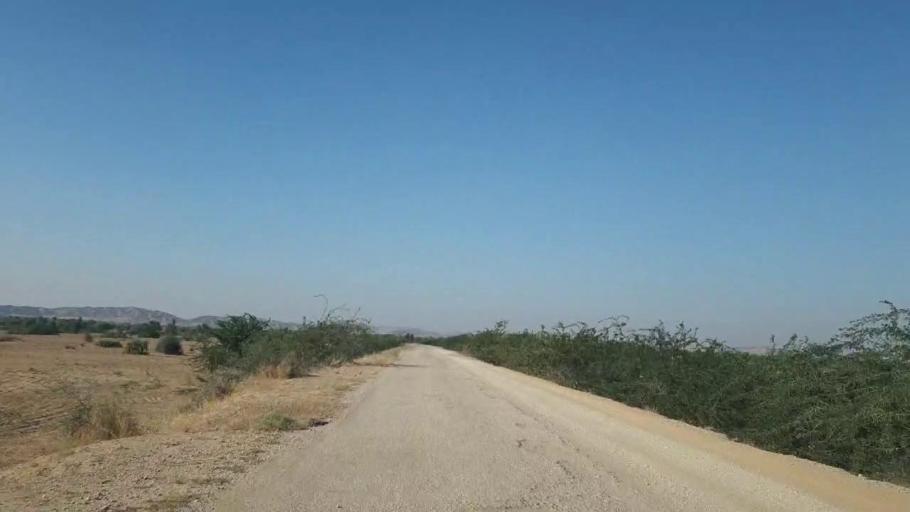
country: PK
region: Sindh
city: Malir Cantonment
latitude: 25.3359
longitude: 67.5712
